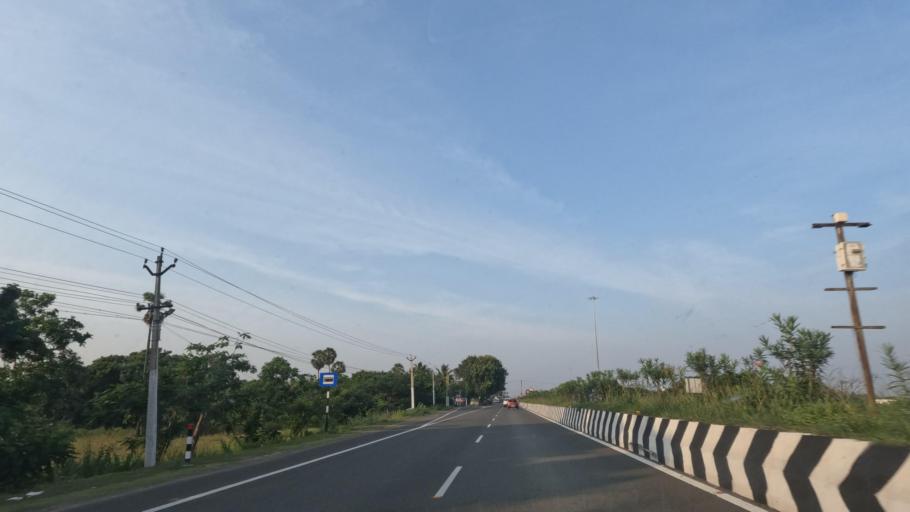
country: IN
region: Tamil Nadu
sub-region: Kancheepuram
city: Mamallapuram
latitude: 12.6879
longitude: 80.2166
